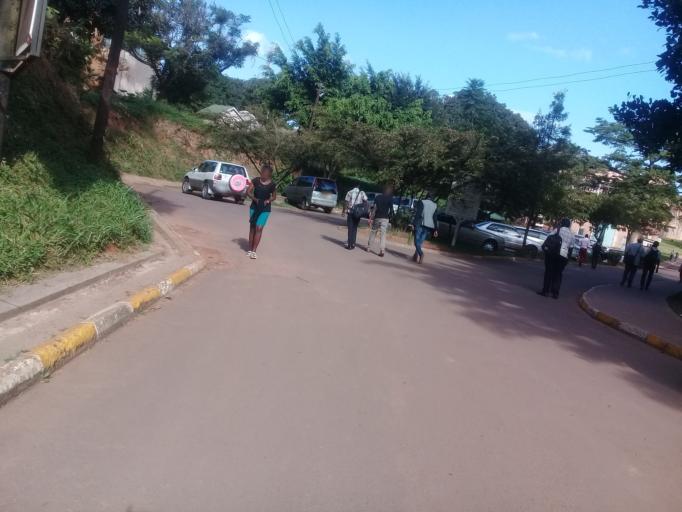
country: UG
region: Central Region
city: Kampala Central Division
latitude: 0.3369
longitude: 32.5648
